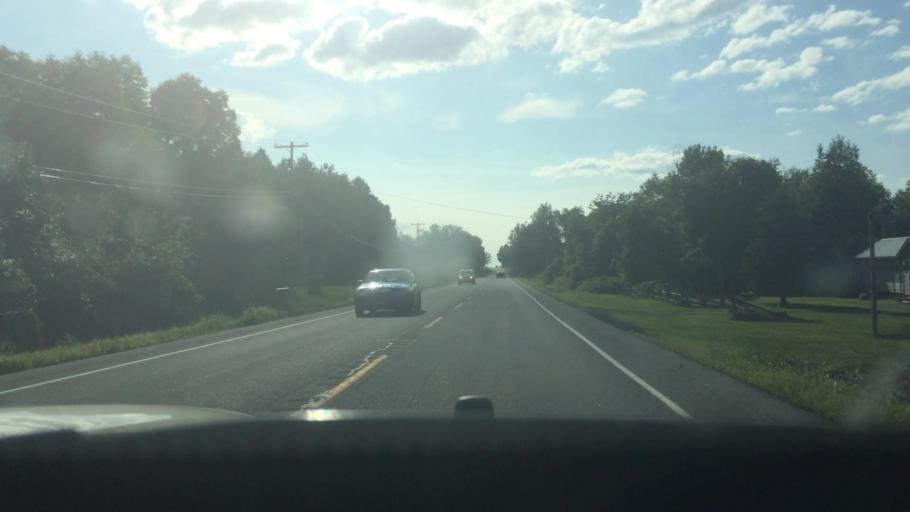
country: US
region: New York
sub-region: St. Lawrence County
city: Potsdam
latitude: 44.6895
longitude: -74.7345
